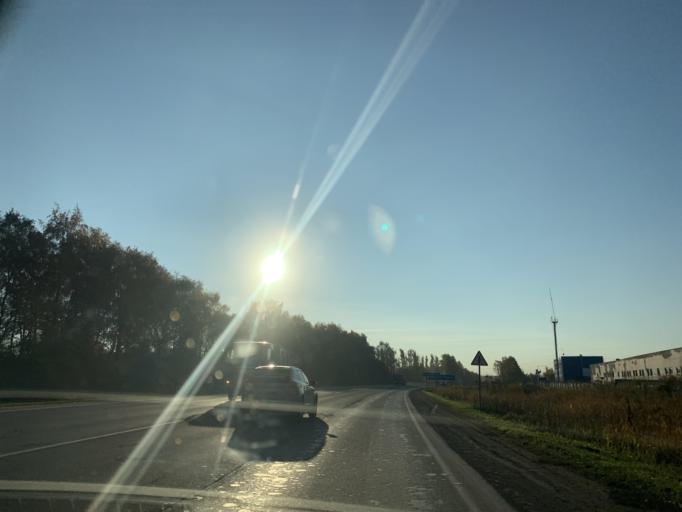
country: RU
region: Jaroslavl
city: Konstantinovskiy
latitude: 57.7401
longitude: 39.7277
